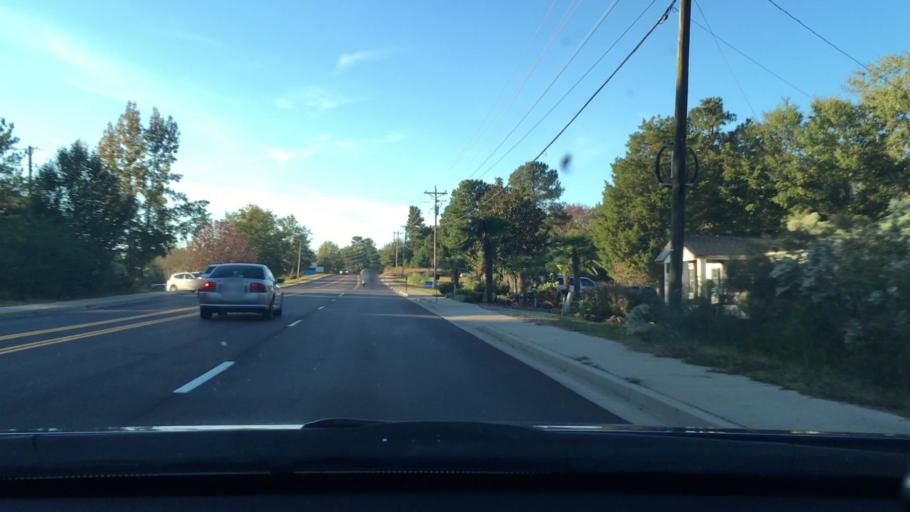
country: US
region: South Carolina
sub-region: Lexington County
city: Irmo
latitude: 34.1156
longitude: -81.1663
